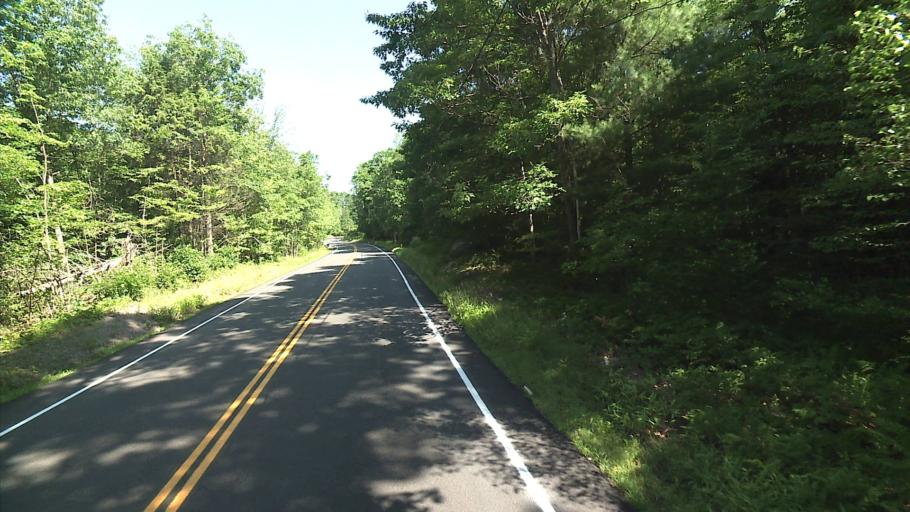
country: US
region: Connecticut
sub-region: Litchfield County
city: Terryville
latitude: 41.7371
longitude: -73.0167
